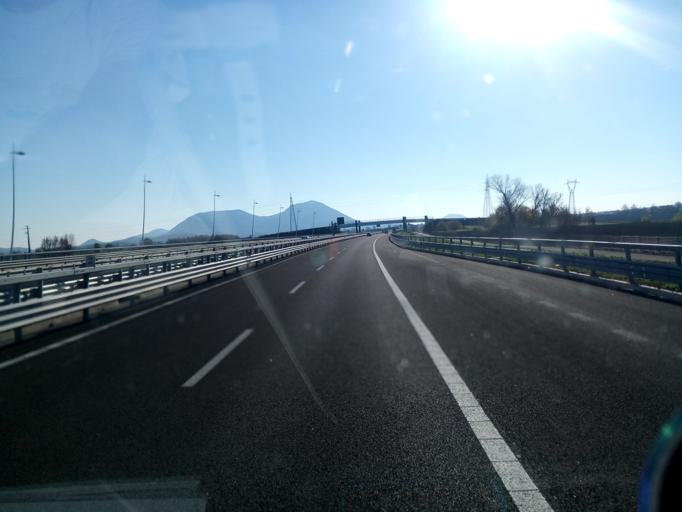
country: IT
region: Veneto
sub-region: Provincia di Vicenza
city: Villaganzerla
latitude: 45.4347
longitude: 11.6369
